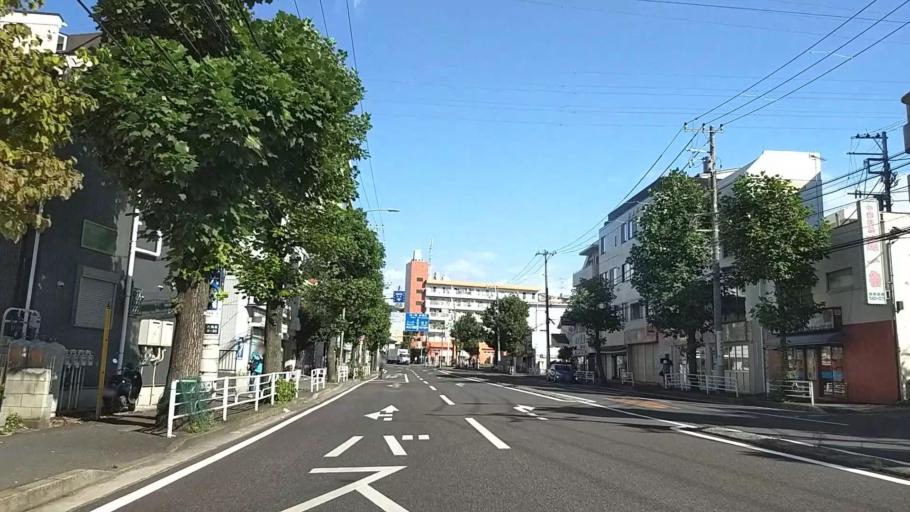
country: JP
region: Kanagawa
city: Yokohama
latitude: 35.4935
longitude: 139.6200
